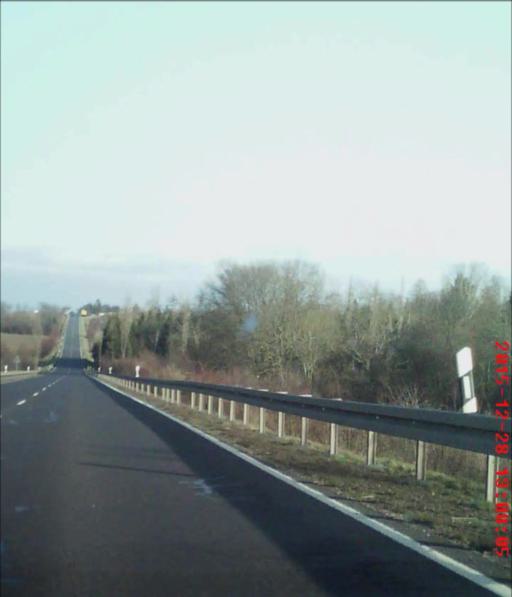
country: DE
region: Thuringia
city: Niederrossla
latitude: 51.0246
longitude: 11.4877
